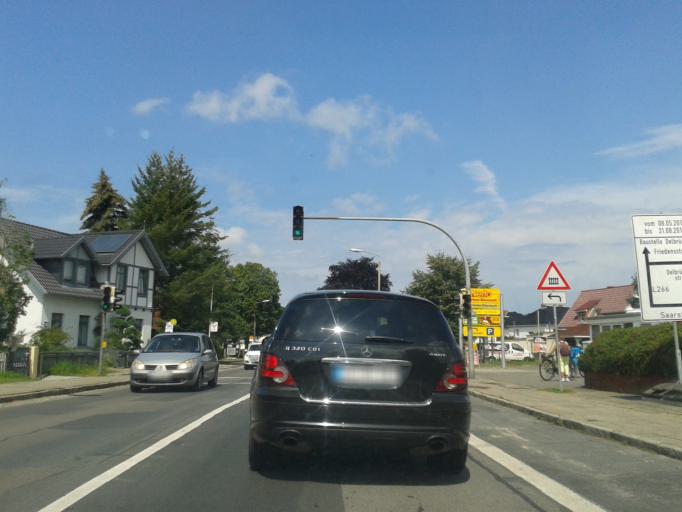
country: DE
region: Mecklenburg-Vorpommern
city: Seebad Heringsdorf
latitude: 53.9424
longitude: 14.1809
